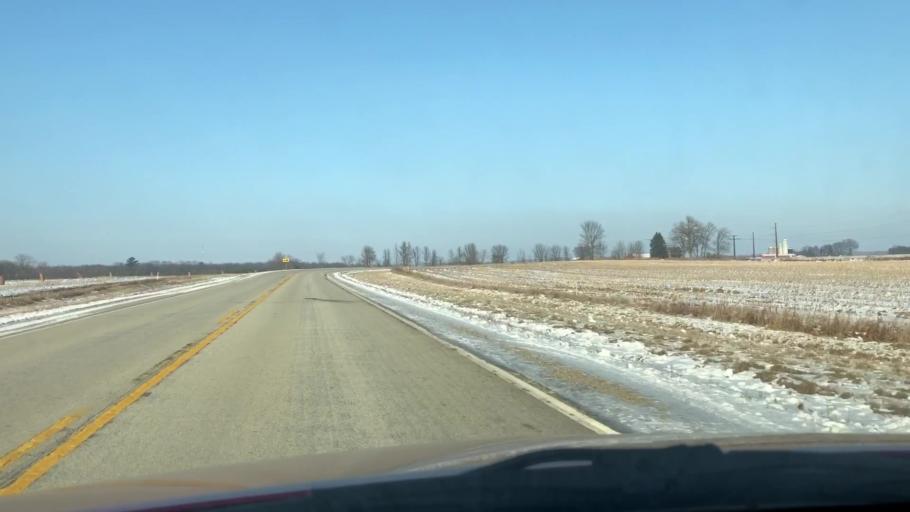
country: US
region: Wisconsin
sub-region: Outagamie County
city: Seymour
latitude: 44.4403
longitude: -88.3611
